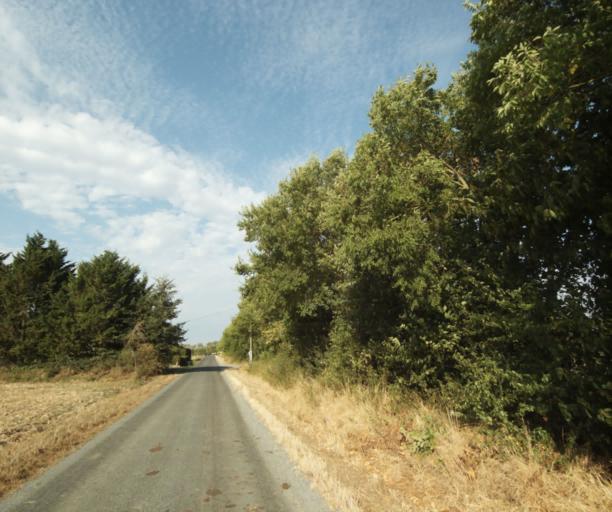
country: FR
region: Poitou-Charentes
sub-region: Departement de la Charente-Maritime
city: Muron
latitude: 45.9858
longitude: -0.8351
